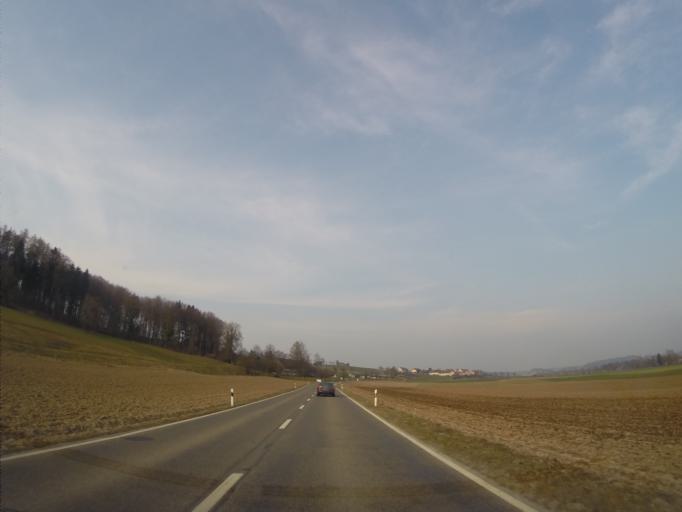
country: CH
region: Zurich
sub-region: Bezirk Winterthur
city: Neftenbach / Dorf Neftenbach
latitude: 47.5352
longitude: 8.6703
